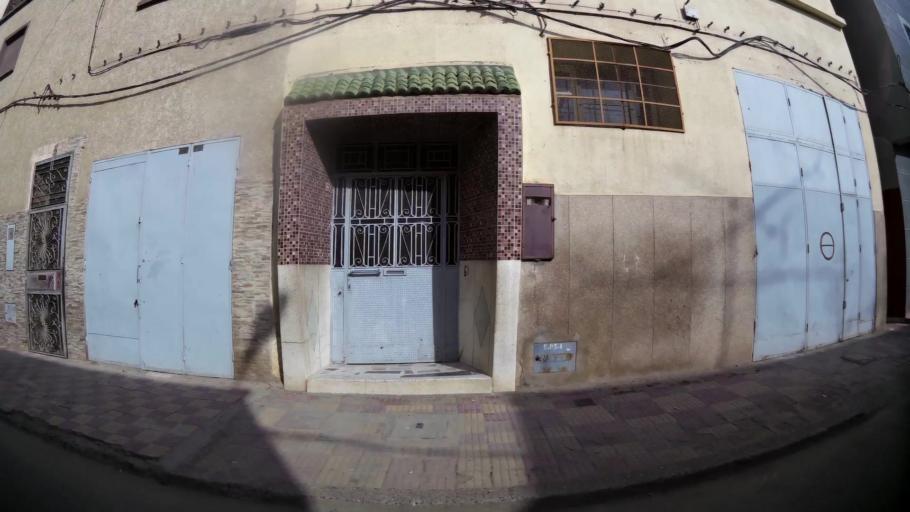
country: MA
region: Oriental
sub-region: Oujda-Angad
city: Oujda
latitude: 34.6909
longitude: -1.9068
